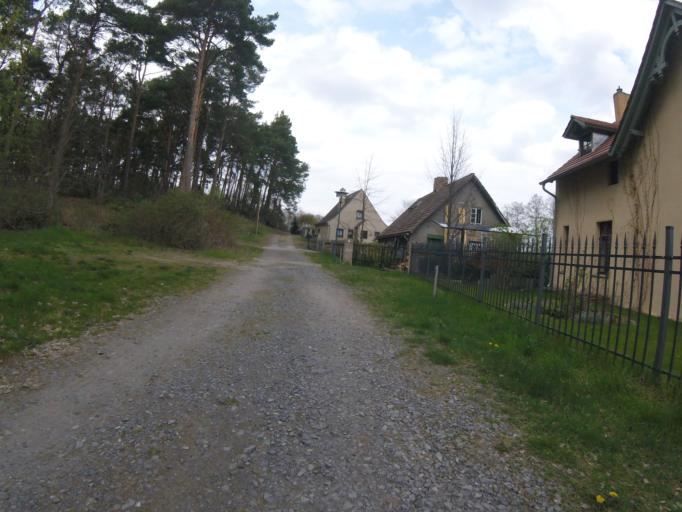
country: DE
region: Brandenburg
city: Gross Koris
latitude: 52.1728
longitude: 13.6606
